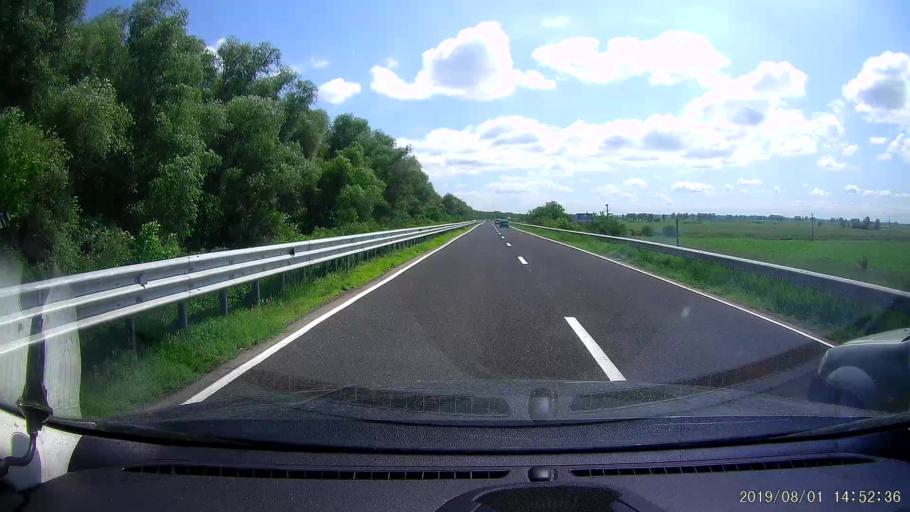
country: RO
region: Braila
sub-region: Comuna Vadeni
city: Vadeni
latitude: 45.3517
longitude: 28.0099
